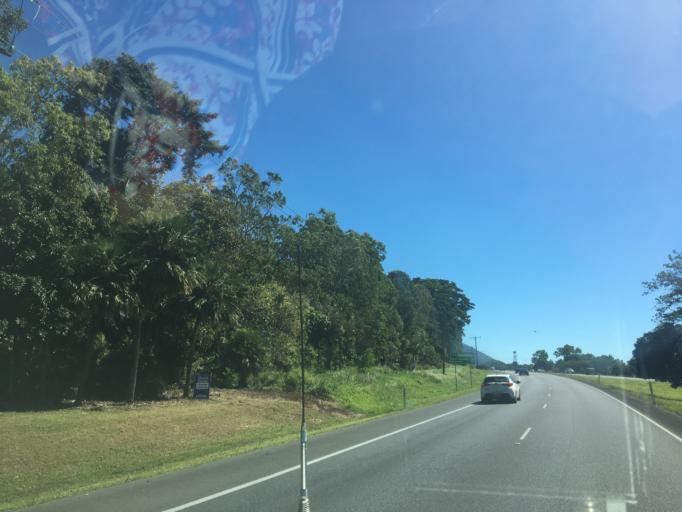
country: AU
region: Queensland
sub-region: Cairns
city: Trinity Beach
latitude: -16.8086
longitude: 145.6921
